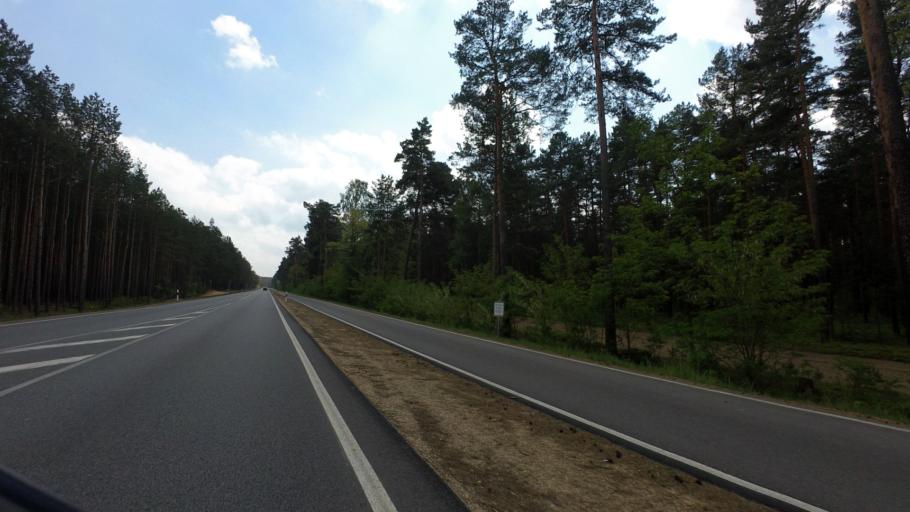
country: DE
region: Saxony
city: Rietschen
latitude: 51.4302
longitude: 14.7857
